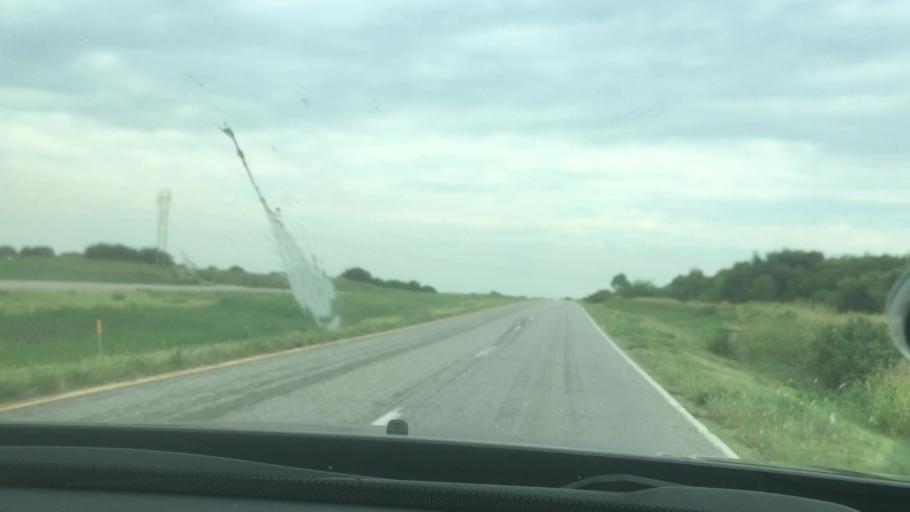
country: US
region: Oklahoma
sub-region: Pontotoc County
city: Ada
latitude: 34.6877
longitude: -96.7528
